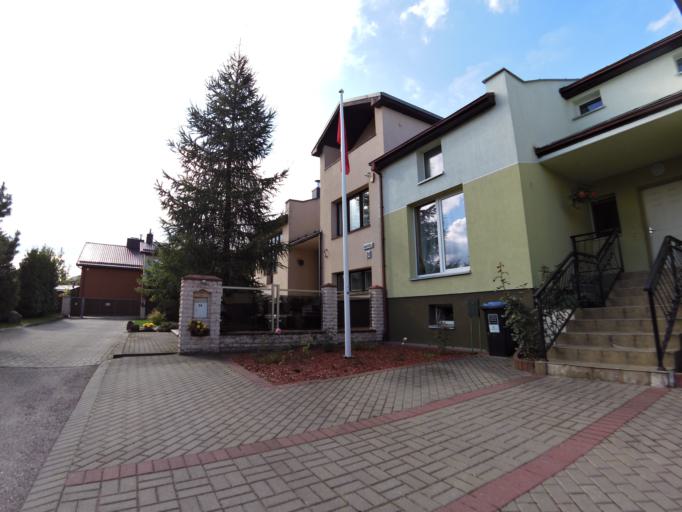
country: LT
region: Vilnius County
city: Pilaite
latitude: 54.7008
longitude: 25.1662
